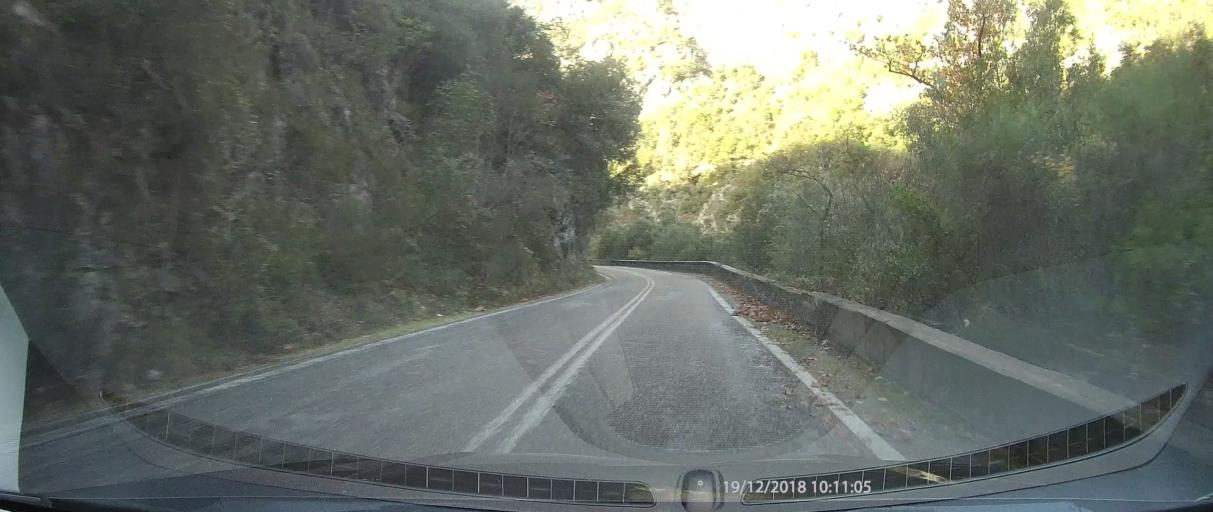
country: GR
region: Peloponnese
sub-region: Nomos Messinias
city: Kalamata
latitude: 37.0993
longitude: 22.1799
